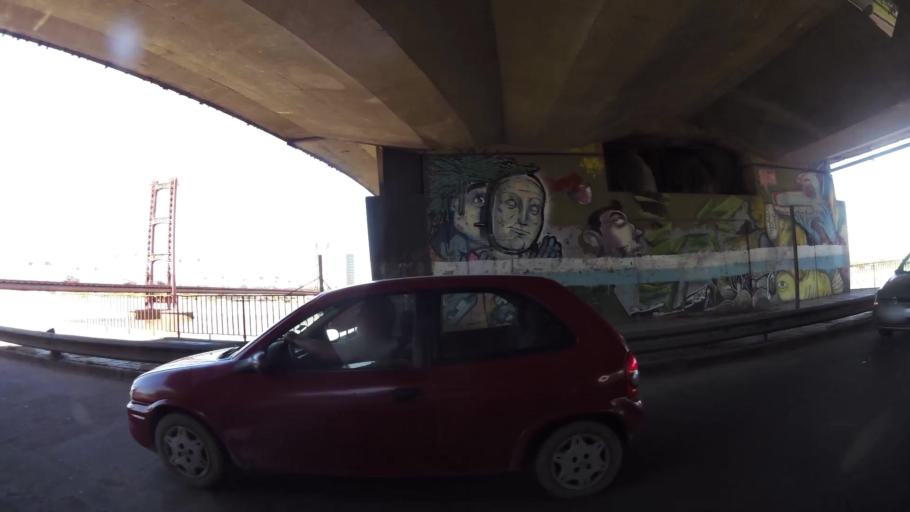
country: AR
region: Santa Fe
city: Santa Fe de la Vera Cruz
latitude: -31.6404
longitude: -60.6832
